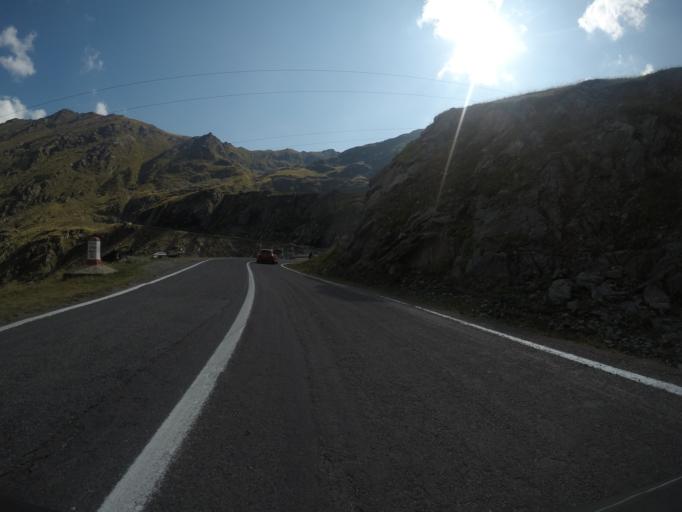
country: RO
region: Sibiu
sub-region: Comuna Cartisoara
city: Cartisoara
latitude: 45.6091
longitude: 24.6141
